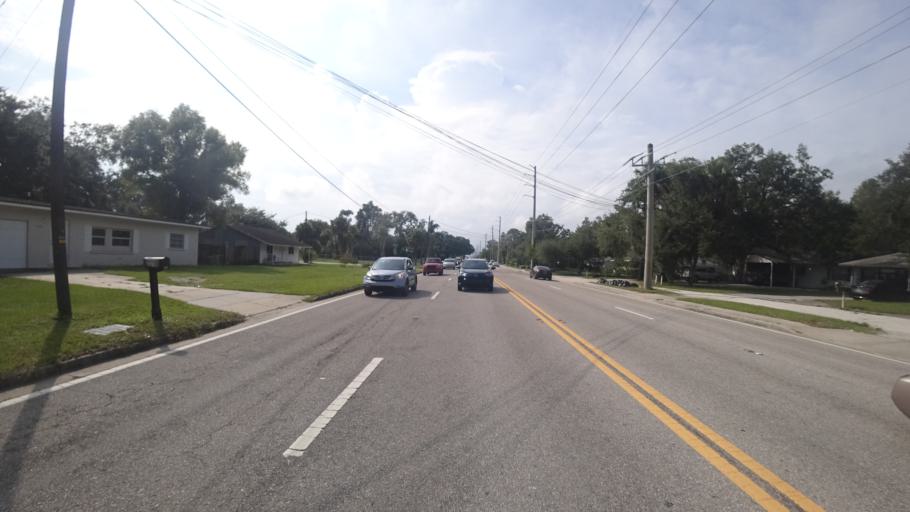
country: US
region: Florida
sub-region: Manatee County
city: South Bradenton
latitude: 27.4477
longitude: -82.5850
